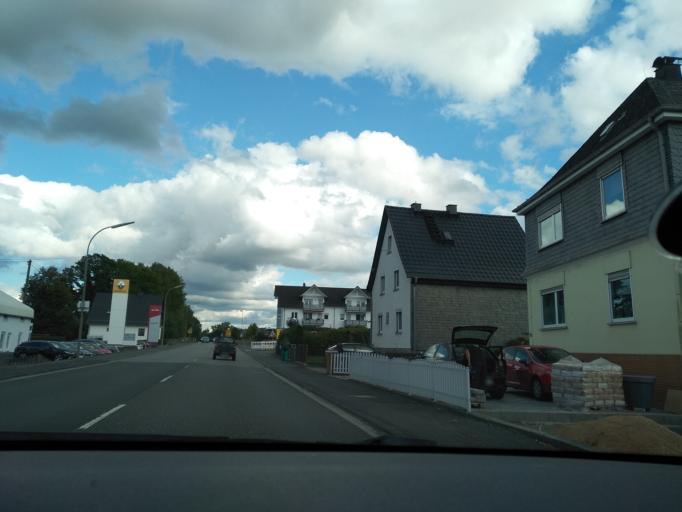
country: DE
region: Hesse
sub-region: Regierungsbezirk Giessen
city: Haiger
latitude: 50.7462
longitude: 8.1877
